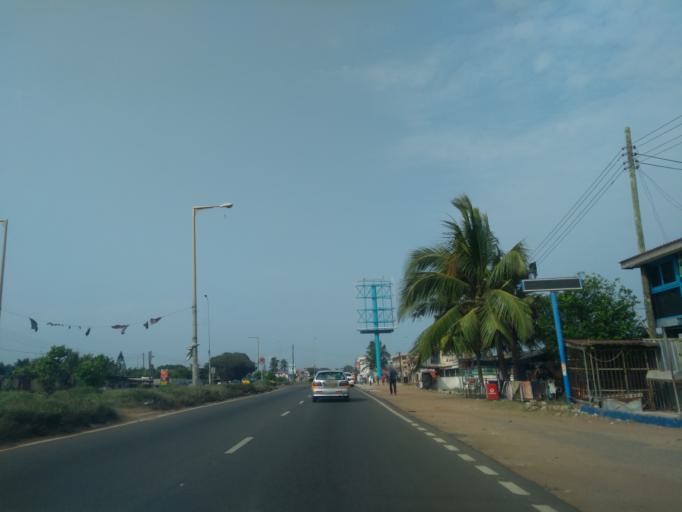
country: GH
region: Greater Accra
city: Accra
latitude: 5.5553
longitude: -0.1694
